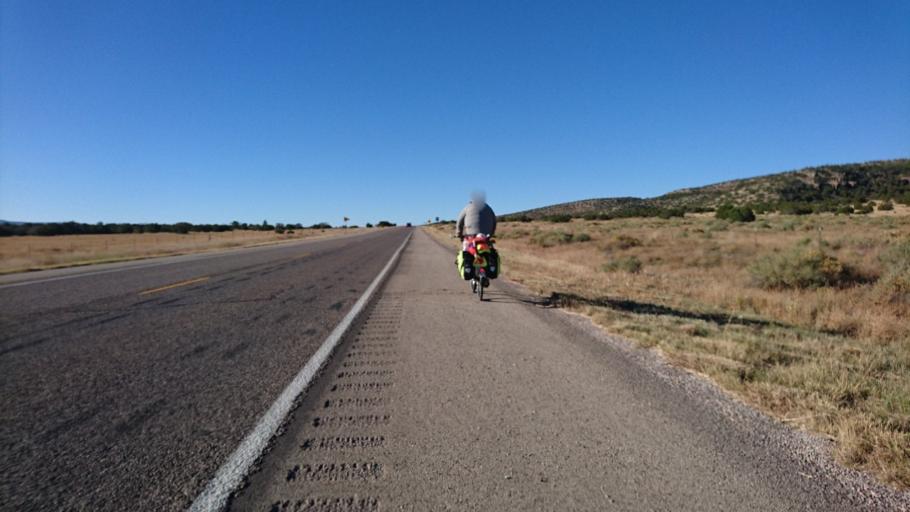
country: US
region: New Mexico
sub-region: Cibola County
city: Grants
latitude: 34.9837
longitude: -107.9046
